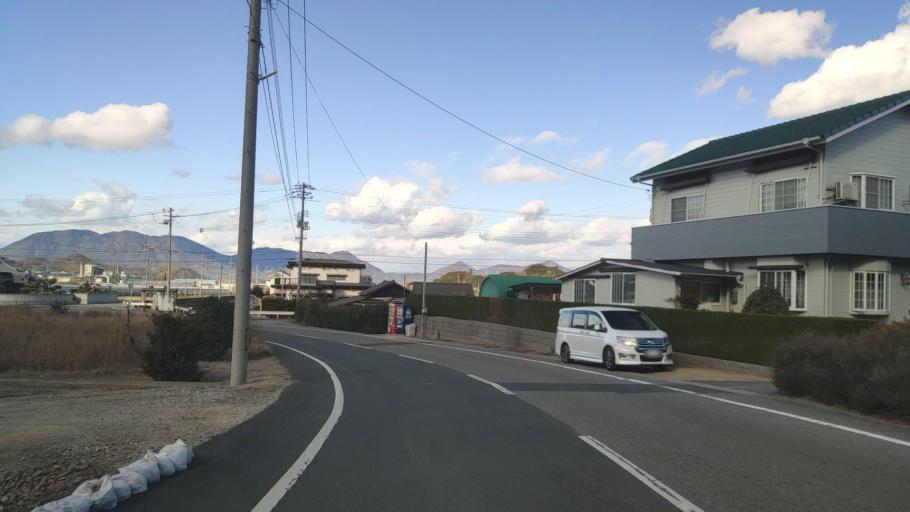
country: JP
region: Hiroshima
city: Innoshima
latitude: 34.2103
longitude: 133.1231
